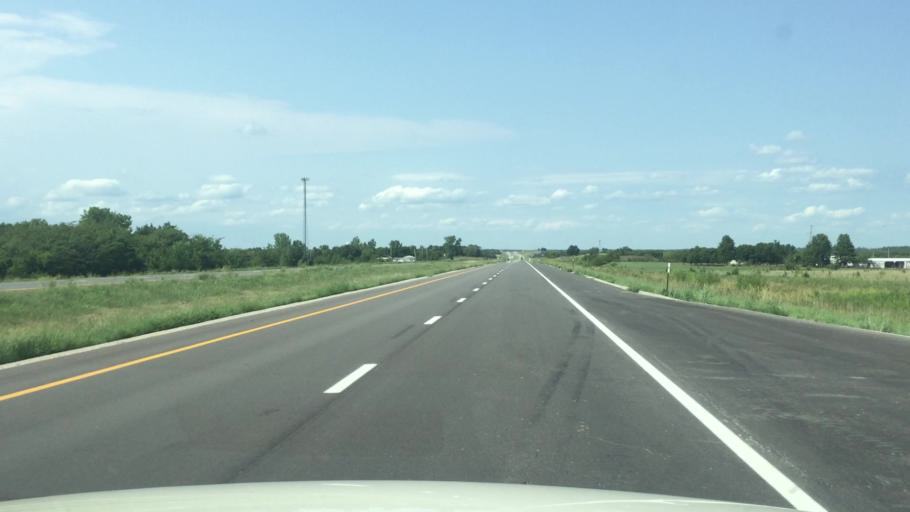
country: US
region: Kansas
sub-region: Linn County
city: La Cygne
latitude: 38.3696
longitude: -94.6873
